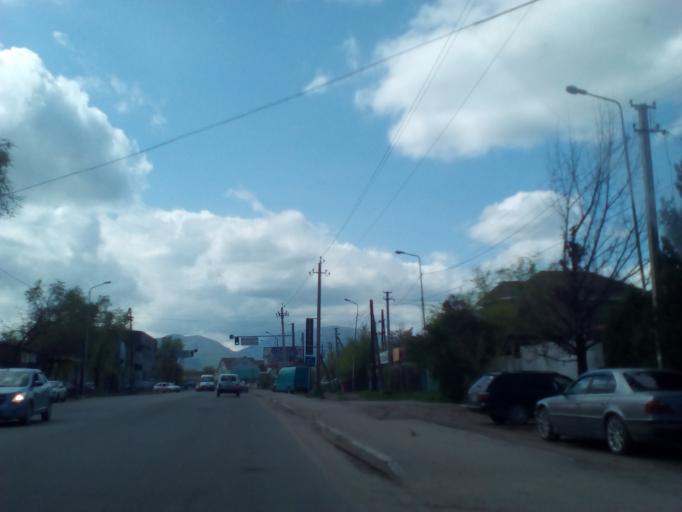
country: KZ
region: Almaty Oblysy
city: Burunday
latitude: 43.2084
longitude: 76.6388
